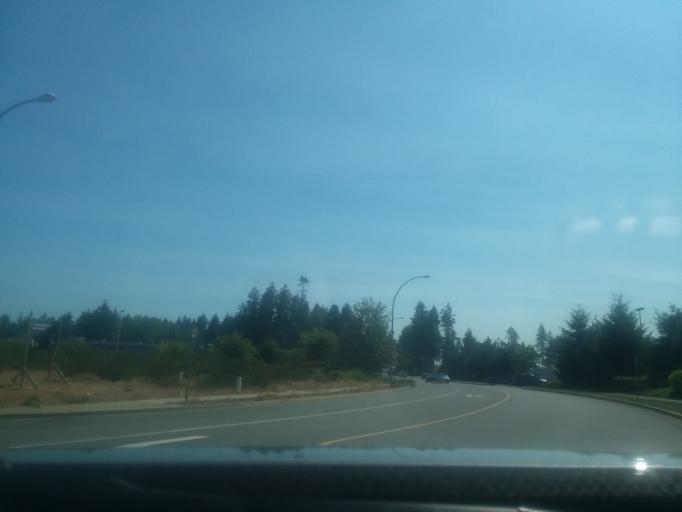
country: CA
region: British Columbia
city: Courtenay
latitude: 49.7145
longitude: -124.9632
